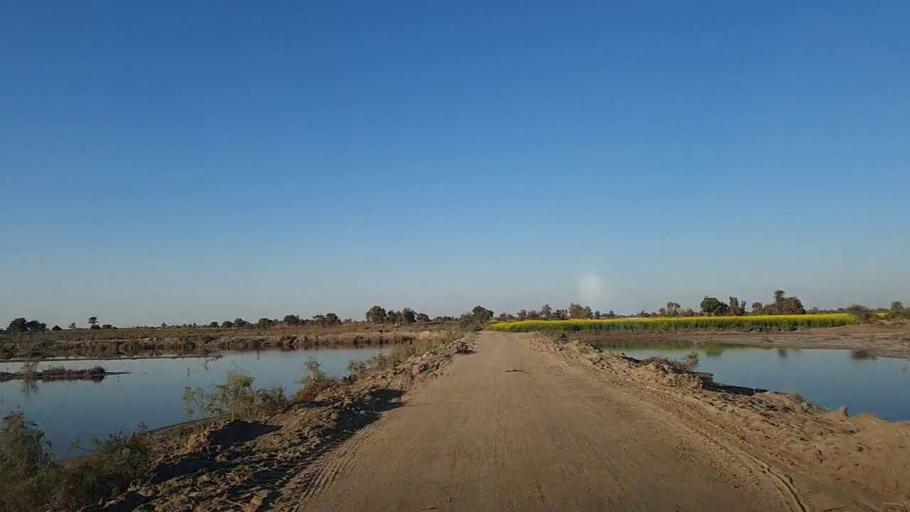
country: PK
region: Sindh
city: Sanghar
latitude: 26.1470
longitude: 68.9265
